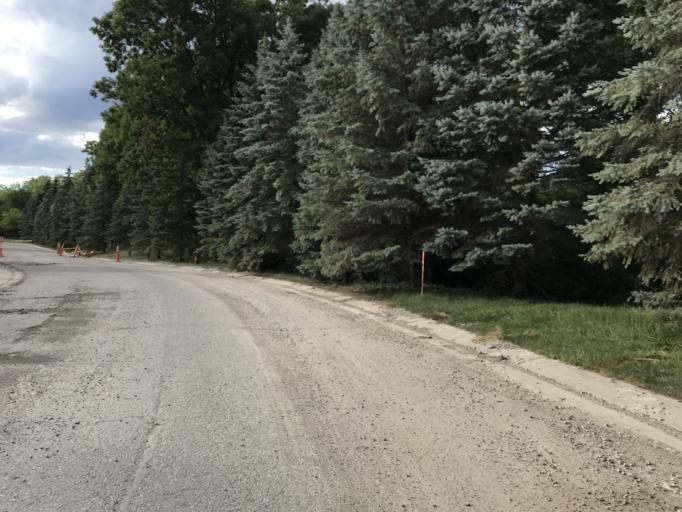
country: US
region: Michigan
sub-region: Oakland County
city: Franklin
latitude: 42.4695
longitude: -83.3204
